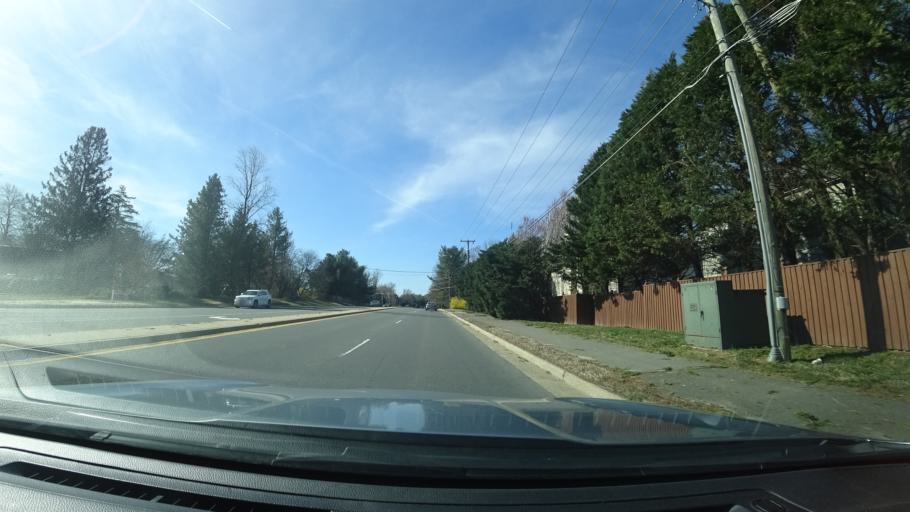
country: US
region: Virginia
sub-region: Fairfax County
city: Oak Hill
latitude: 38.9216
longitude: -77.3747
